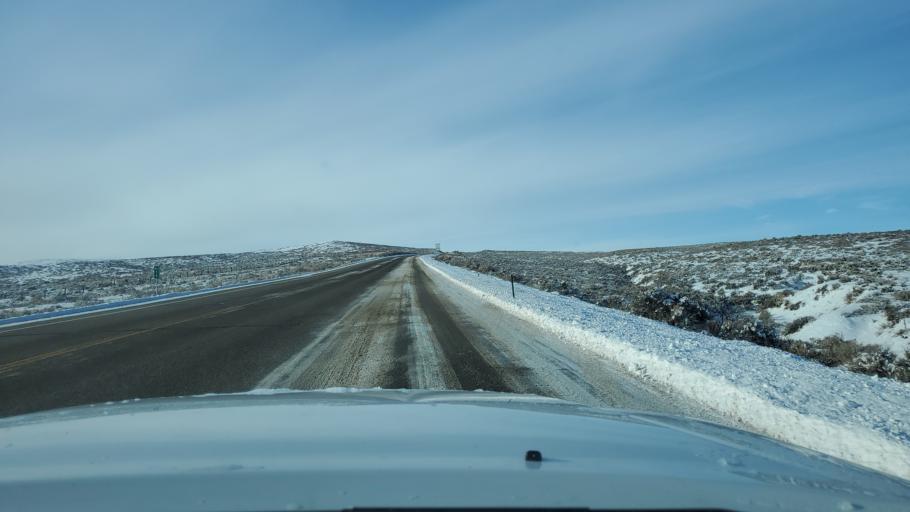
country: US
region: Colorado
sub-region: Rio Blanco County
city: Meeker
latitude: 40.5121
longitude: -108.1069
